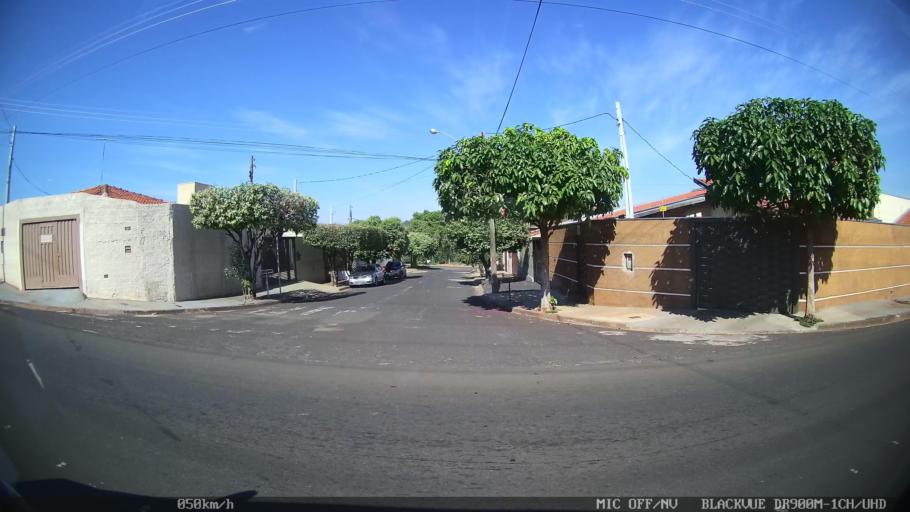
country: BR
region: Sao Paulo
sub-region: Sao Jose Do Rio Preto
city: Sao Jose do Rio Preto
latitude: -20.7630
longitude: -49.3653
